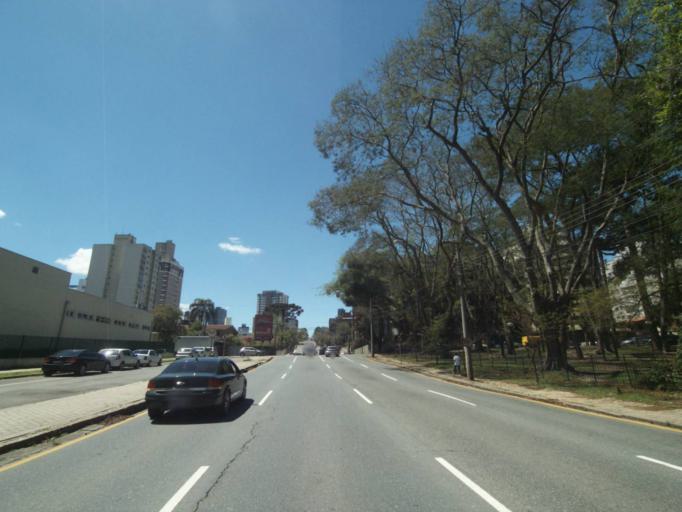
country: BR
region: Parana
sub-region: Curitiba
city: Curitiba
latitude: -25.4052
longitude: -49.2499
